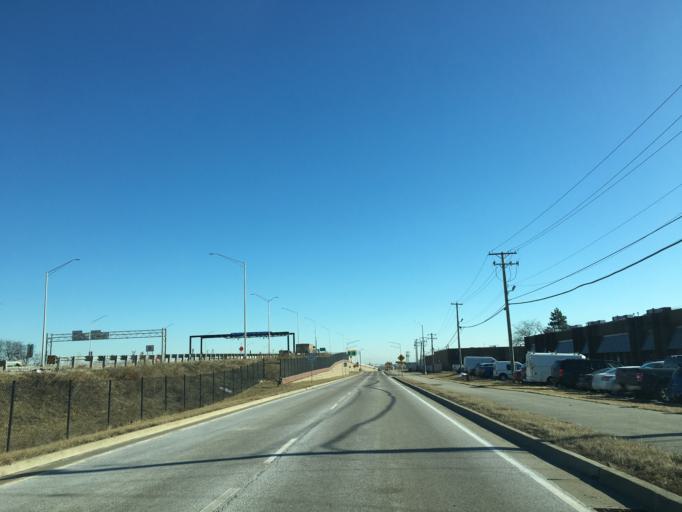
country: US
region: Illinois
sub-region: DuPage County
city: Wood Dale
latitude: 41.9830
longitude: -87.9736
